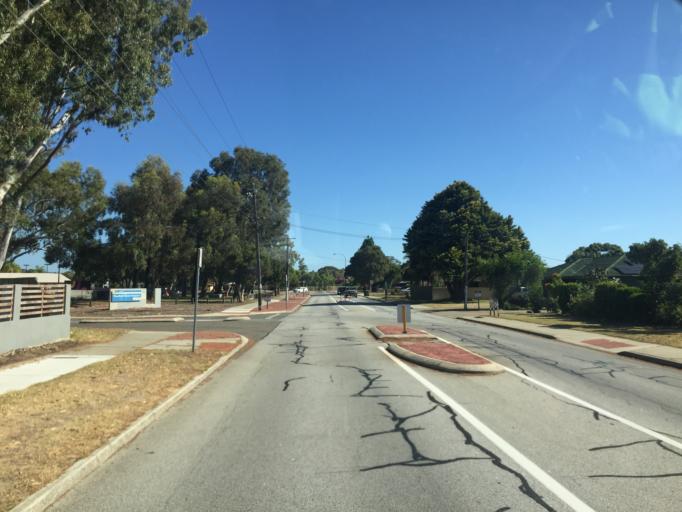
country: AU
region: Western Australia
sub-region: Gosnells
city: Maddington
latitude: -32.0518
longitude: 116.0000
